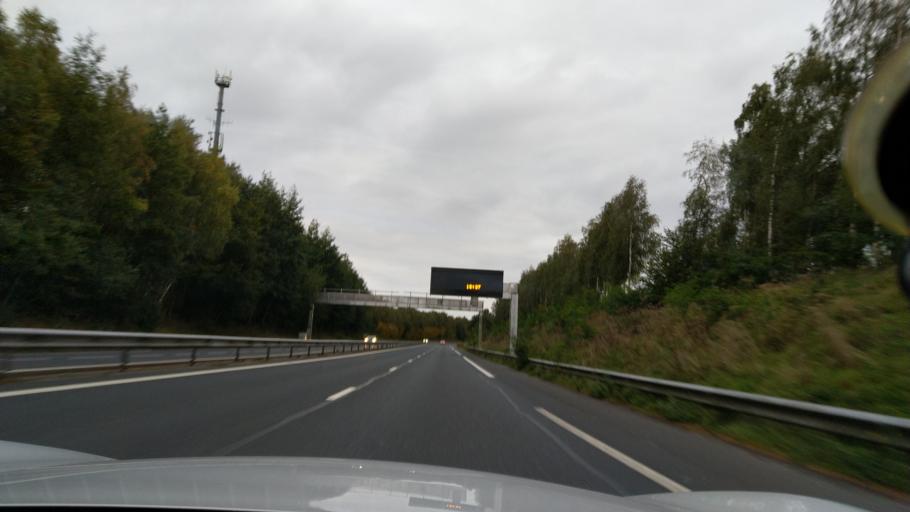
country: FR
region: Haute-Normandie
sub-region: Departement de la Seine-Maritime
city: Saint-Martin-Osmonville
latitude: 49.6437
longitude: 1.2661
